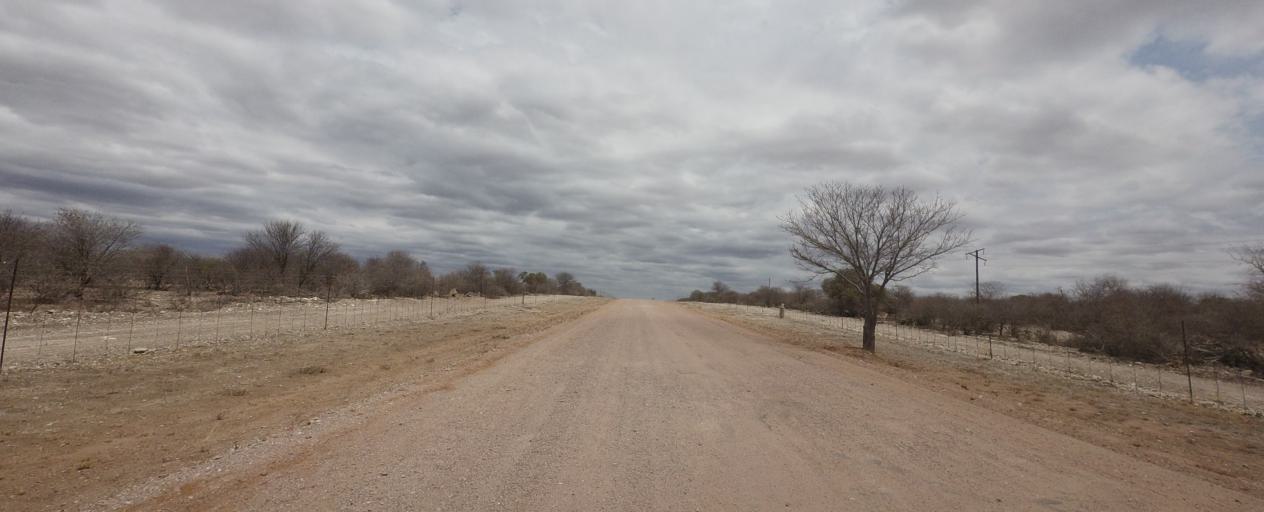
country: BW
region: Central
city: Mathathane
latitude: -22.6911
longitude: 28.6373
